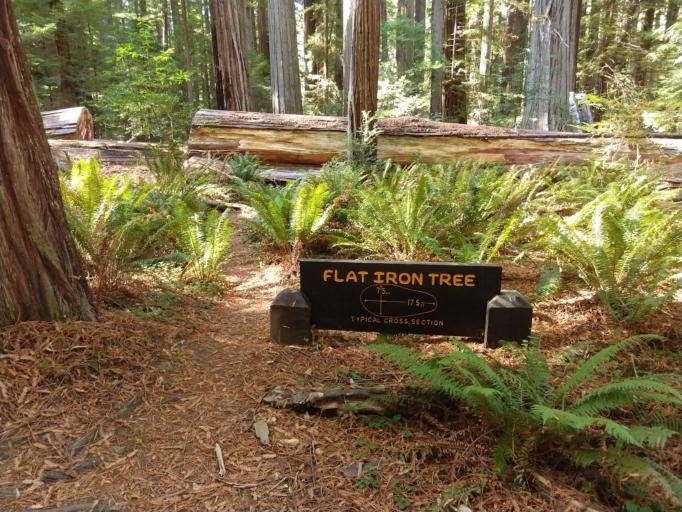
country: US
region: California
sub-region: Humboldt County
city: Rio Dell
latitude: 40.3497
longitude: -123.9927
